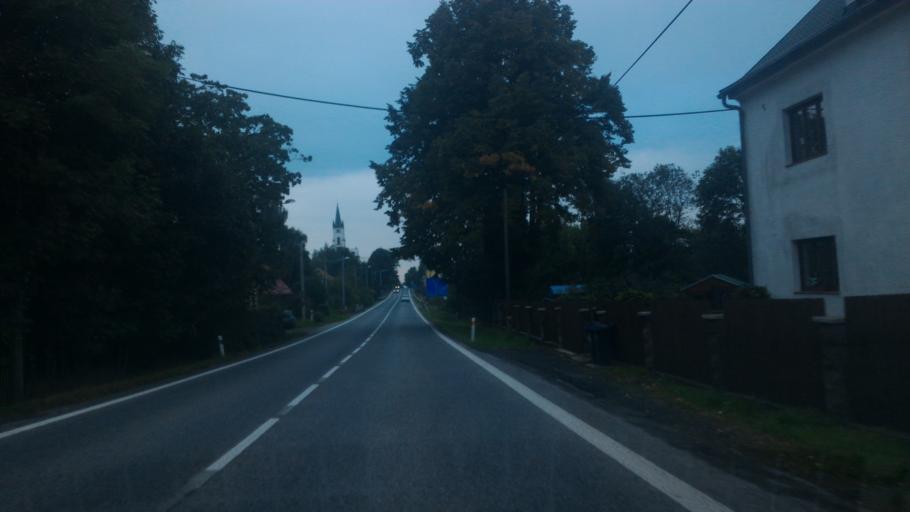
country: CZ
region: Ustecky
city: Dolni Podluzi
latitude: 50.9056
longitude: 14.5681
